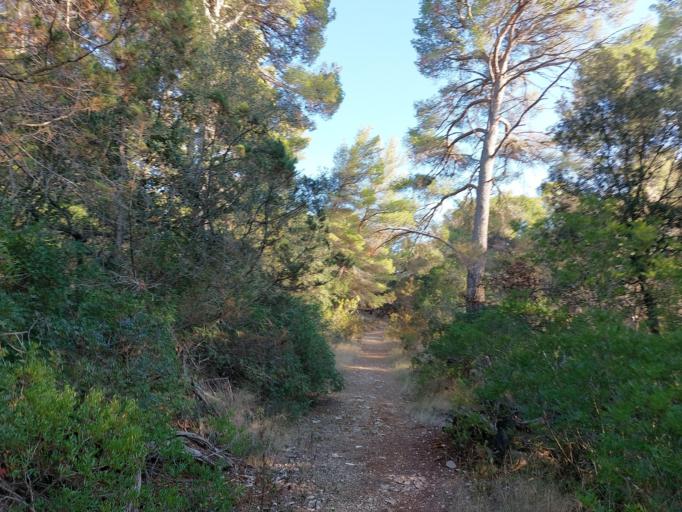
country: HR
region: Dubrovacko-Neretvanska
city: Smokvica
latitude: 42.7732
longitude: 16.7890
